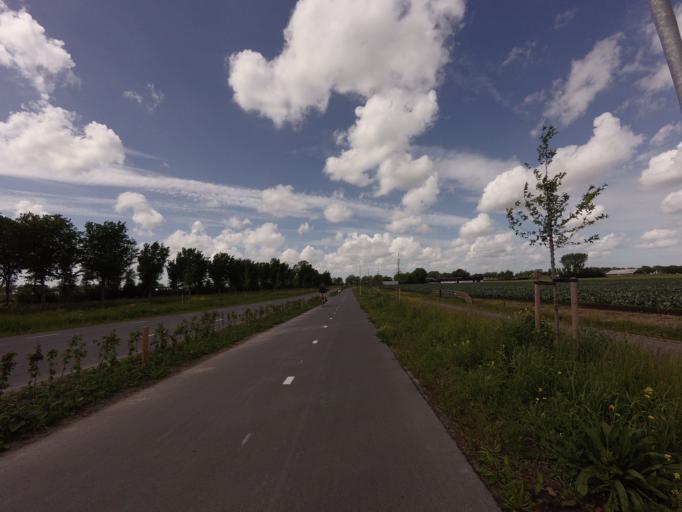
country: NL
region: North Holland
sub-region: Gemeente Hoorn
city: Hoorn
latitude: 52.6827
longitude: 5.0879
